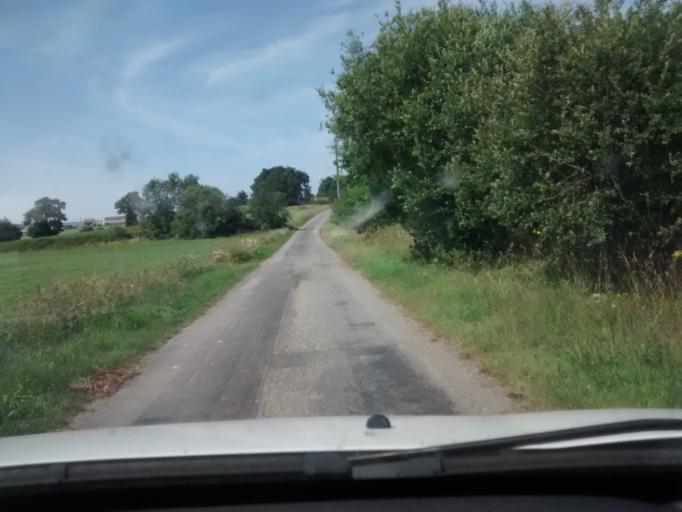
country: FR
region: Brittany
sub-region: Departement d'Ille-et-Vilaine
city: Acigne
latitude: 48.1066
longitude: -1.5598
